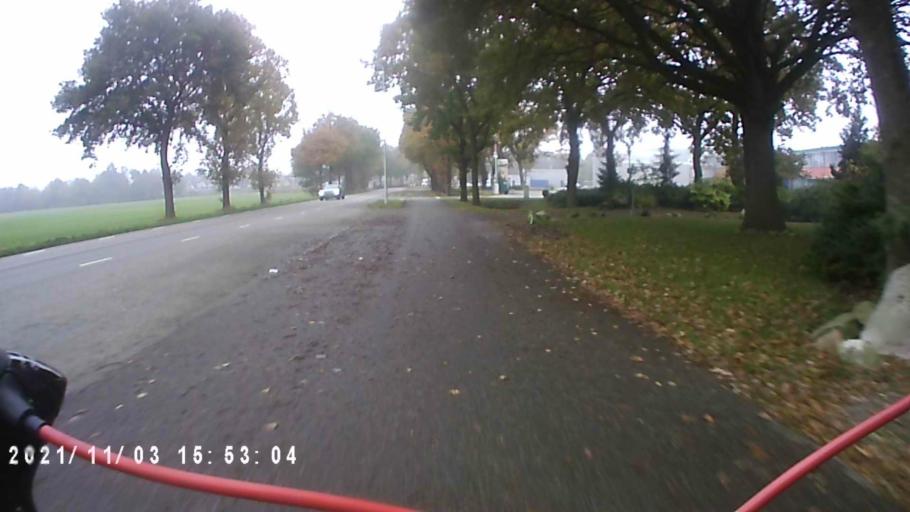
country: NL
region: Groningen
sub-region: Gemeente Leek
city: Leek
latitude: 53.0726
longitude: 6.3317
